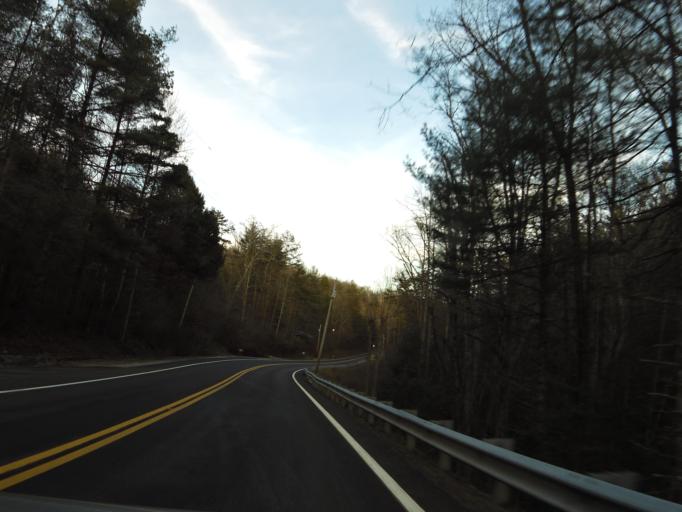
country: US
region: Tennessee
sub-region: Roane County
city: Rockwood
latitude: 35.8735
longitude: -84.7874
